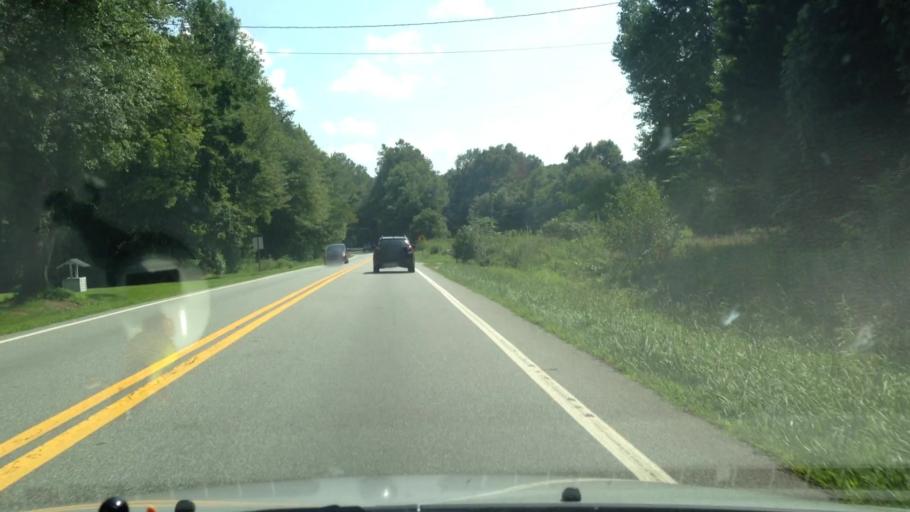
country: US
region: North Carolina
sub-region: Guilford County
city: Oak Ridge
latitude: 36.1814
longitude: -79.9879
